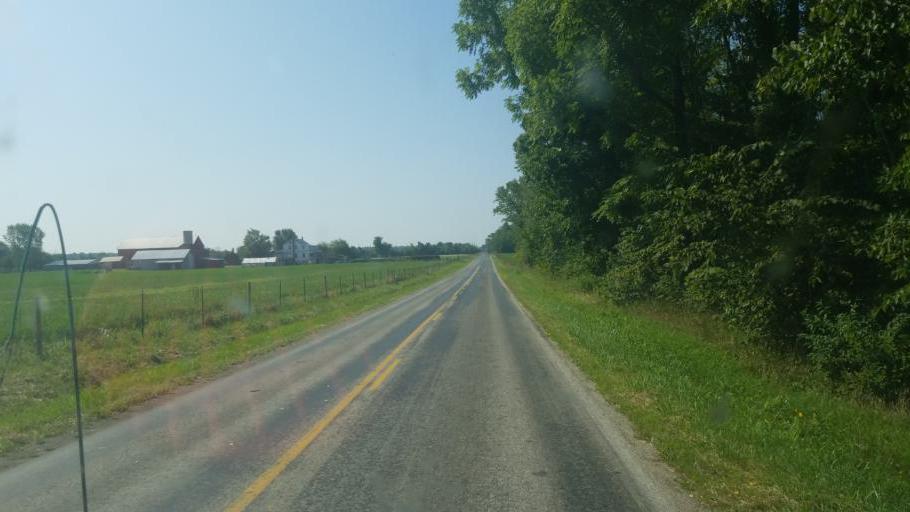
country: US
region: Ohio
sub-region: Wayne County
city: West Salem
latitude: 41.0364
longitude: -82.1821
